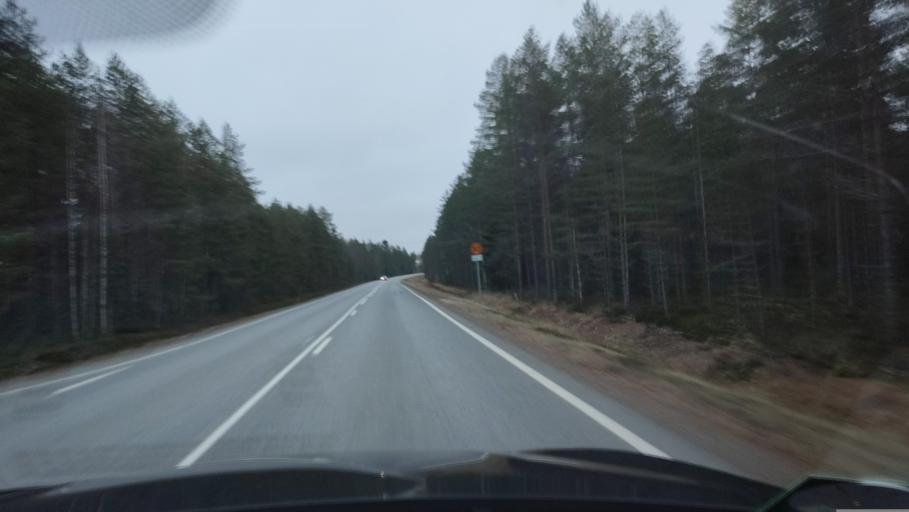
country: FI
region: Southern Ostrobothnia
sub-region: Suupohja
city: Isojoki
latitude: 62.3448
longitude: 21.9595
